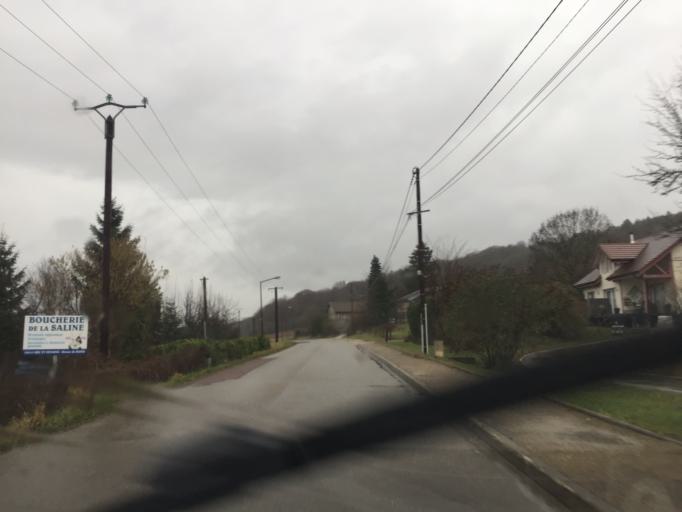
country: FR
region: Franche-Comte
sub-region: Departement du Jura
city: Mouchard
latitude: 46.9813
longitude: 5.7945
